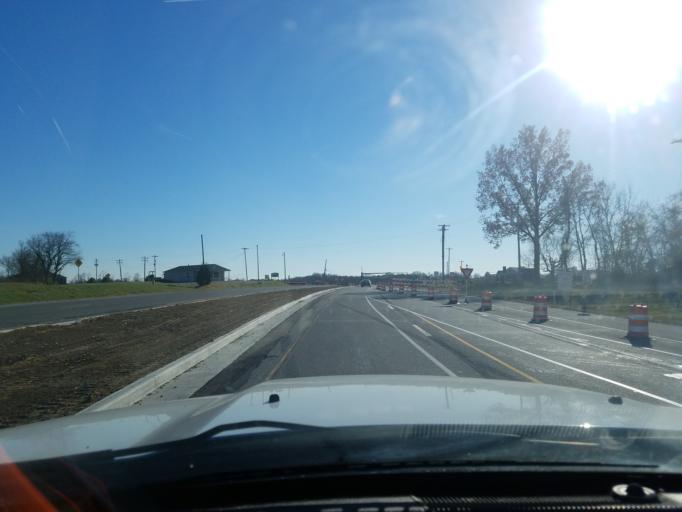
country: US
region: Indiana
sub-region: Clark County
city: Oak Park
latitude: 38.3390
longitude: -85.7067
